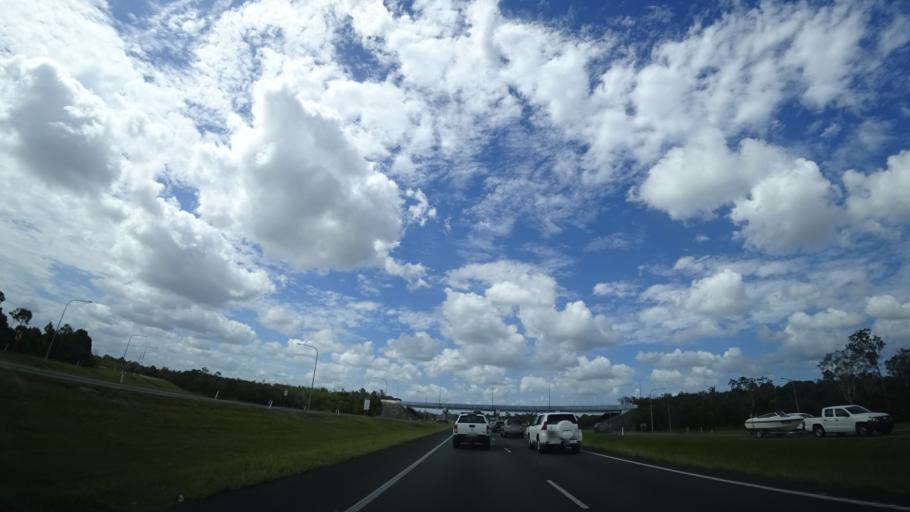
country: AU
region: Queensland
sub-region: Moreton Bay
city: Caboolture
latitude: -27.0735
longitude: 152.9767
